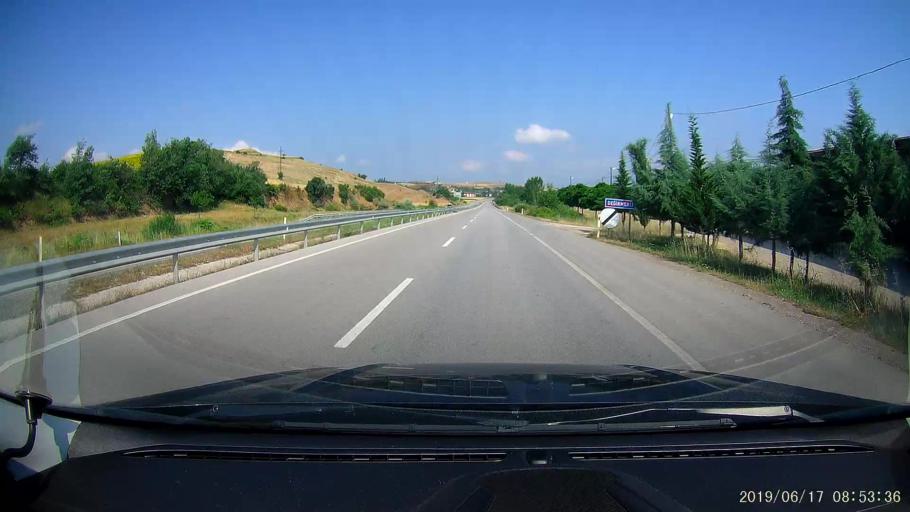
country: TR
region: Tokat
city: Erbaa
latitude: 40.7113
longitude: 36.4780
